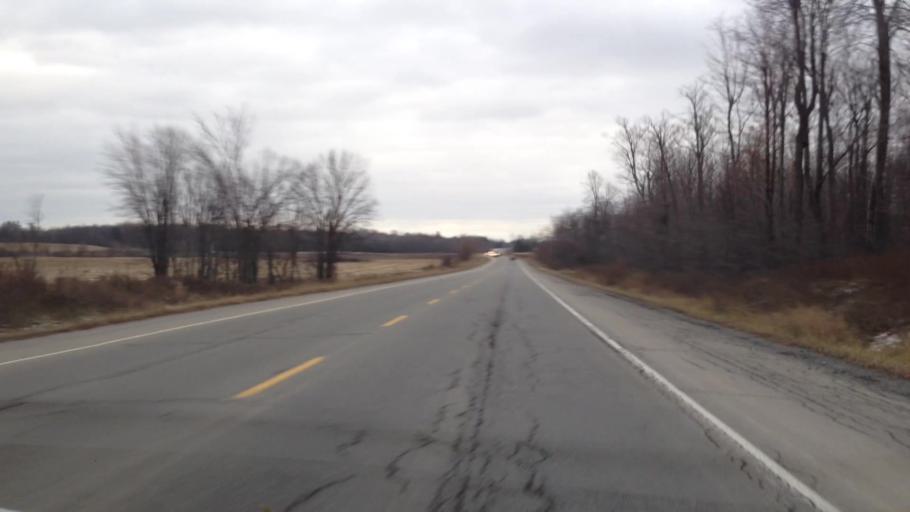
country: CA
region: Ontario
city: Clarence-Rockland
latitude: 45.3906
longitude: -75.3906
